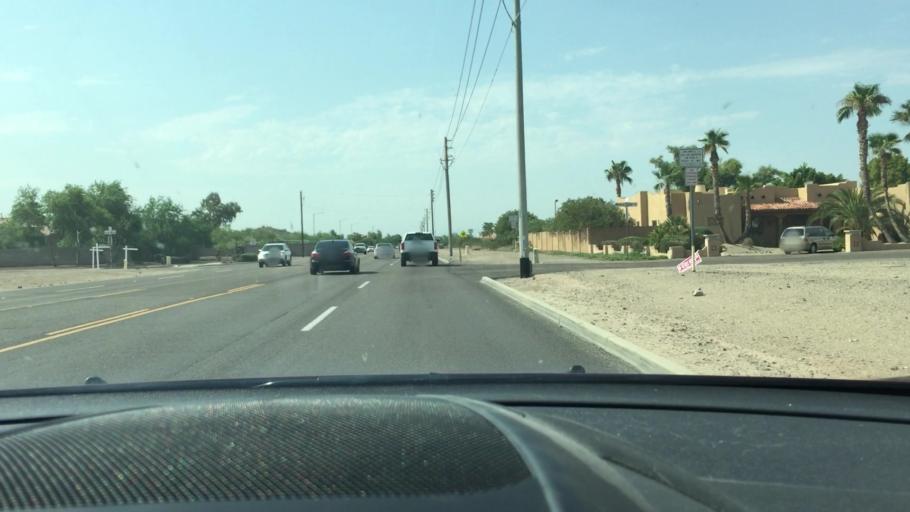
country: US
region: Arizona
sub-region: Maricopa County
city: Sun City
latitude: 33.7020
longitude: -112.2032
